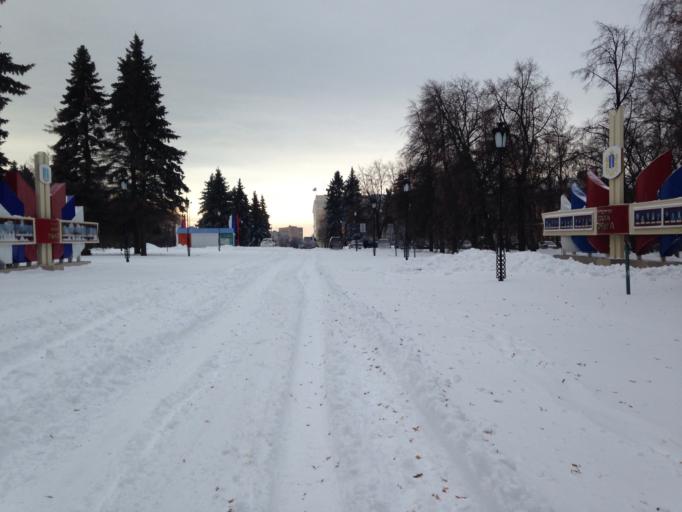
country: RU
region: Ulyanovsk
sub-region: Ulyanovskiy Rayon
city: Ulyanovsk
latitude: 54.3167
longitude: 48.4044
